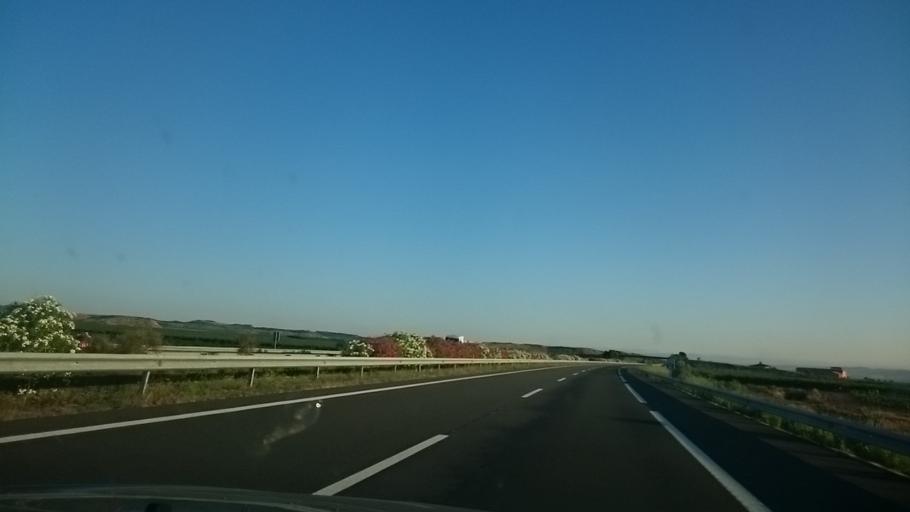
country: ES
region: La Rioja
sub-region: Provincia de La Rioja
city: Aldeanueva de Ebro
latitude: 42.2262
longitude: -1.8983
